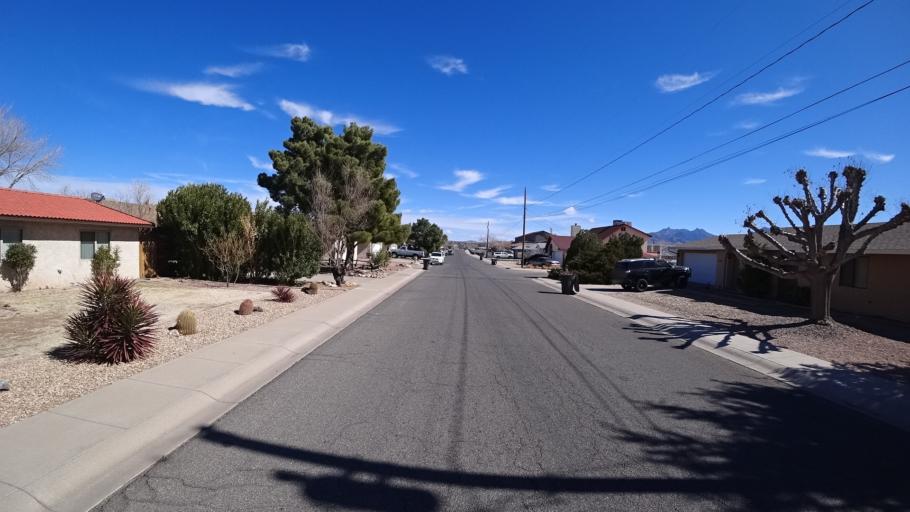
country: US
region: Arizona
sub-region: Mohave County
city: Kingman
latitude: 35.2059
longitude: -114.0383
